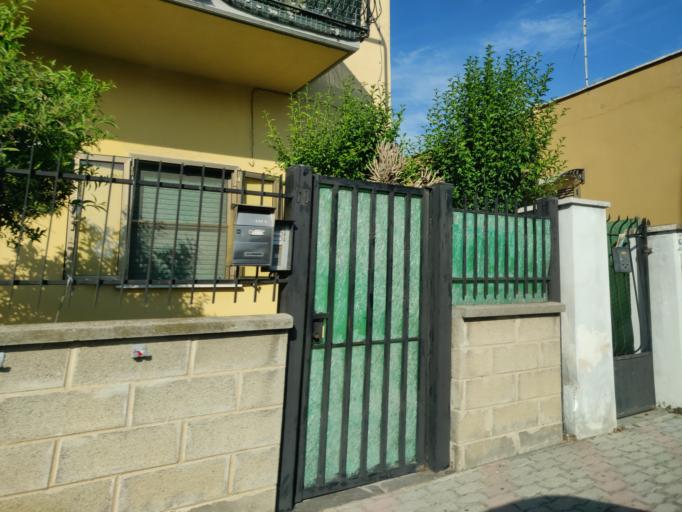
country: IT
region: Latium
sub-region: Citta metropolitana di Roma Capitale
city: Civitavecchia
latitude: 42.0980
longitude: 11.7953
